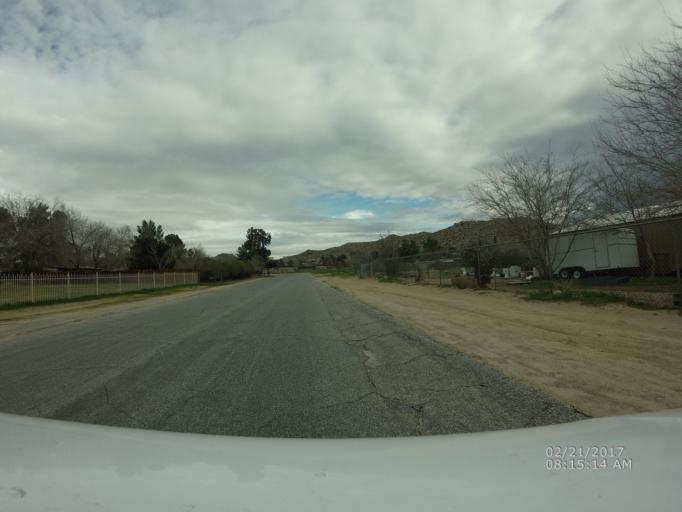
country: US
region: California
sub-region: Los Angeles County
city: Lake Los Angeles
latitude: 34.5972
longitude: -117.8394
